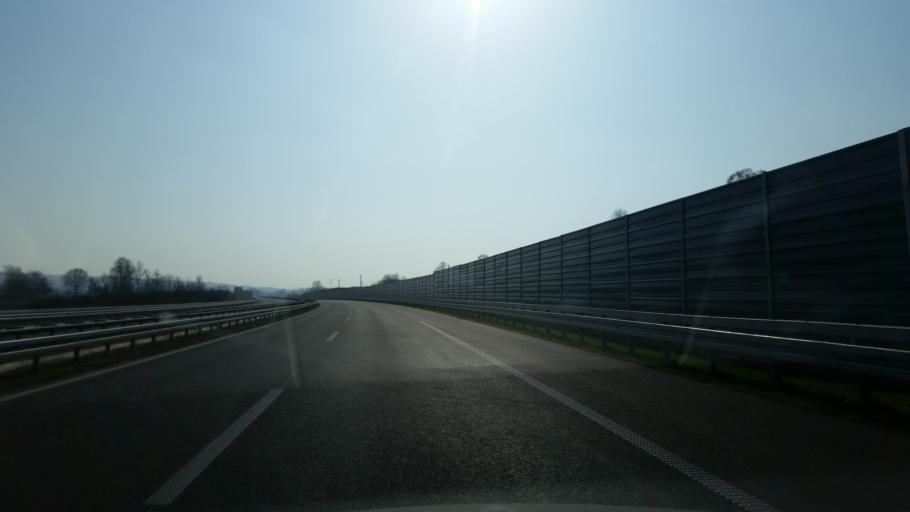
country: RS
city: Prislonica
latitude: 43.9629
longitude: 20.3963
